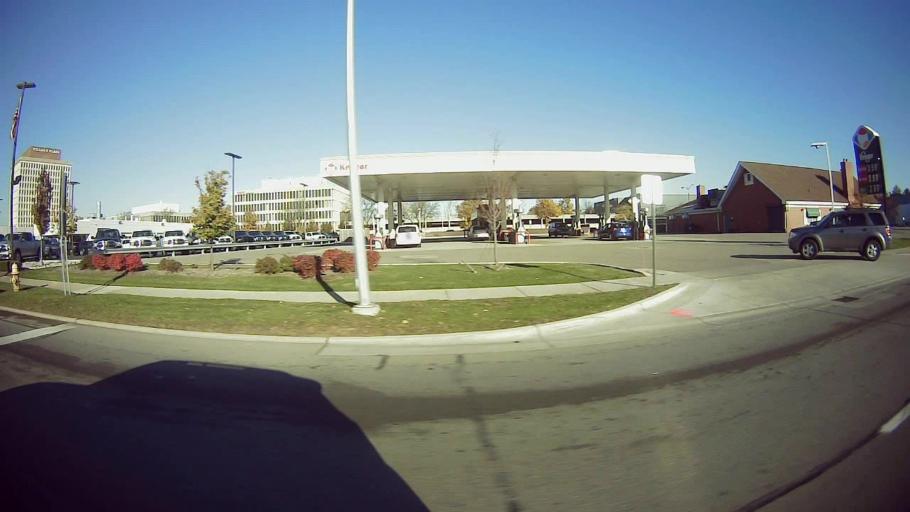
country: US
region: Michigan
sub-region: Wayne County
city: Dearborn Heights
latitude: 42.3029
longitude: -83.2597
